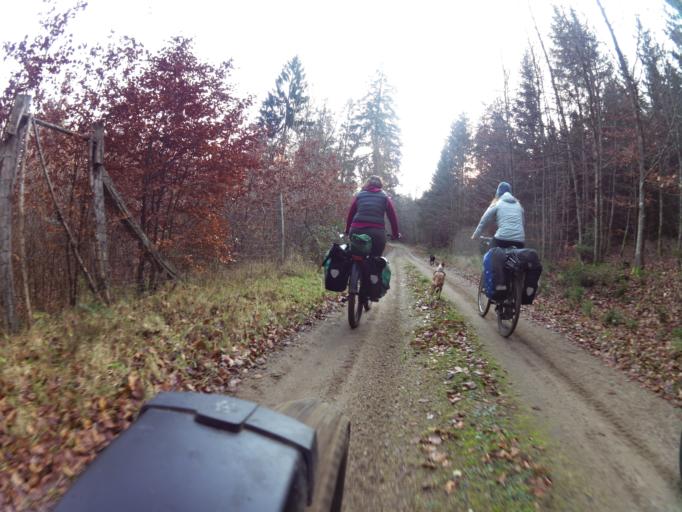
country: PL
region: West Pomeranian Voivodeship
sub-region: Powiat koszalinski
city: Polanow
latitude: 54.1738
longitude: 16.7259
